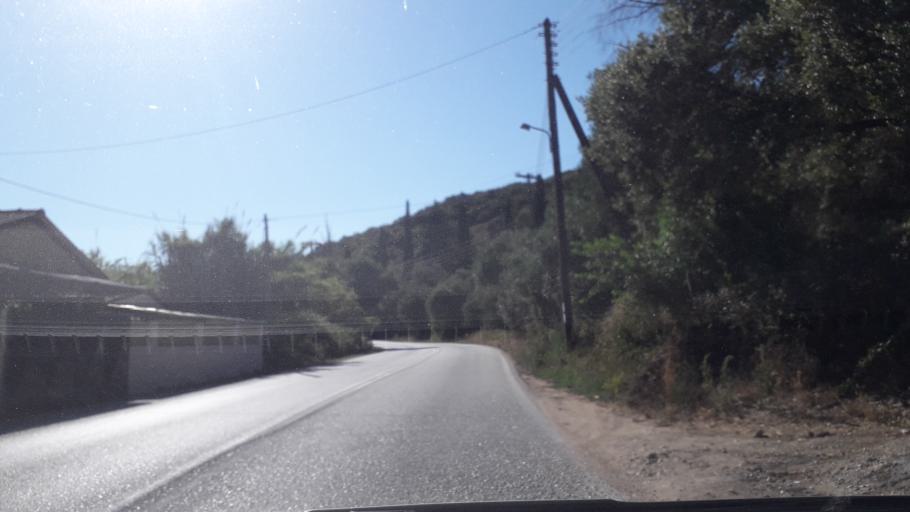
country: GR
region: Ionian Islands
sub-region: Nomos Kerkyras
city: Agios Matthaios
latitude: 39.4768
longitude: 19.9247
